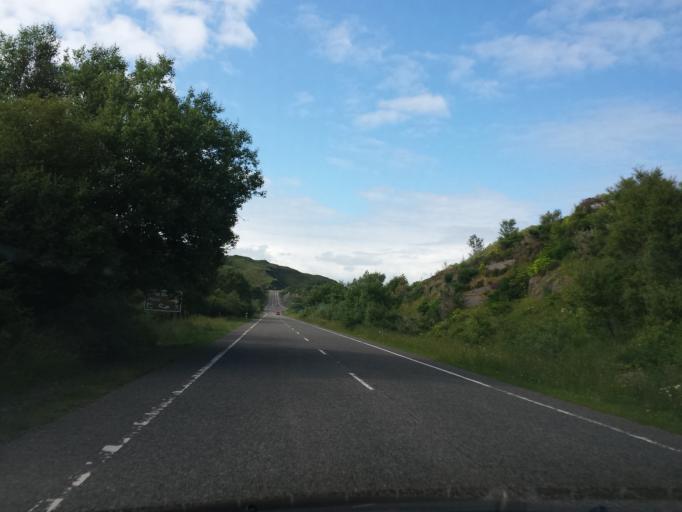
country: GB
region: Scotland
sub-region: Argyll and Bute
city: Isle Of Mull
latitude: 56.9704
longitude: -5.8255
